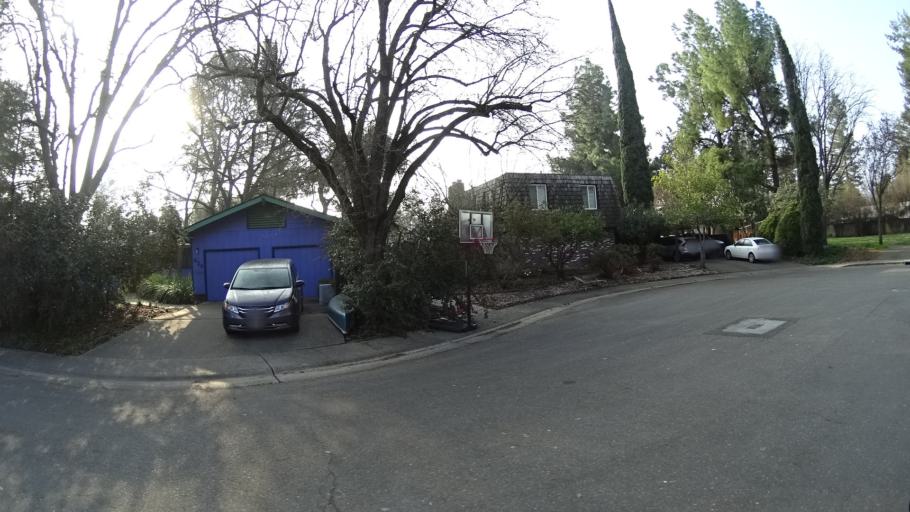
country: US
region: California
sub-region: Yolo County
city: Davis
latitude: 38.5635
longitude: -121.7549
